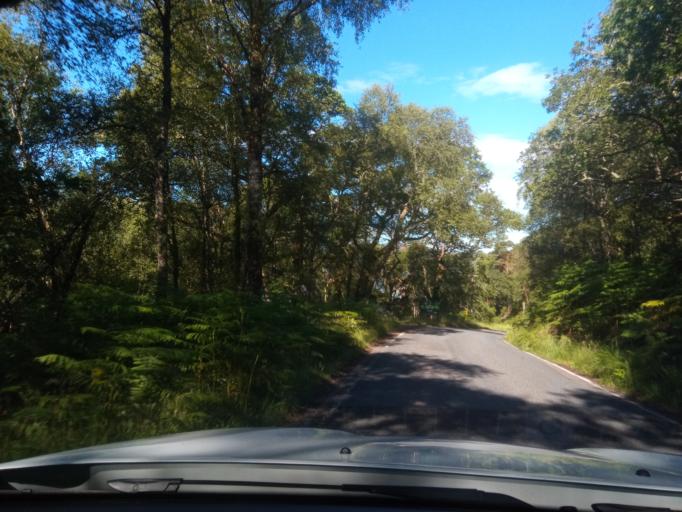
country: GB
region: Scotland
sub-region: Argyll and Bute
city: Isle Of Mull
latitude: 56.6982
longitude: -5.6890
